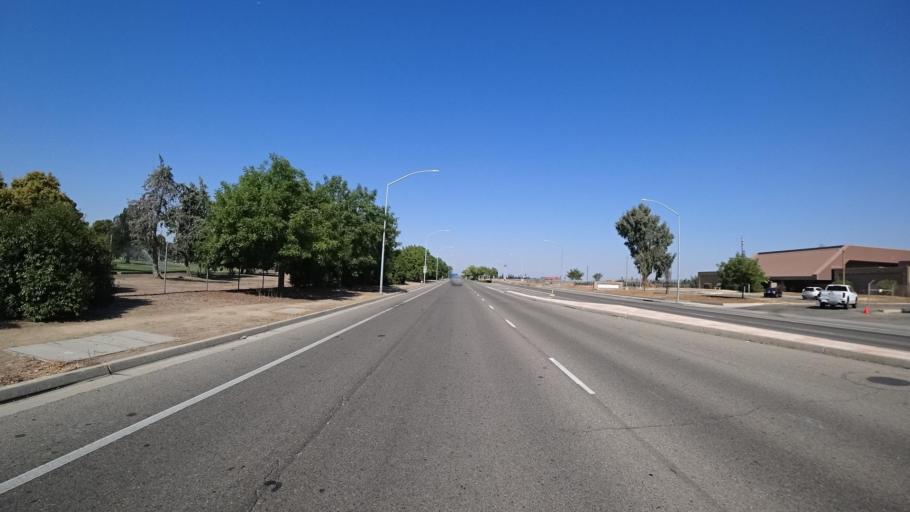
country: US
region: California
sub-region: Fresno County
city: Tarpey Village
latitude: 36.7793
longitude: -119.7013
